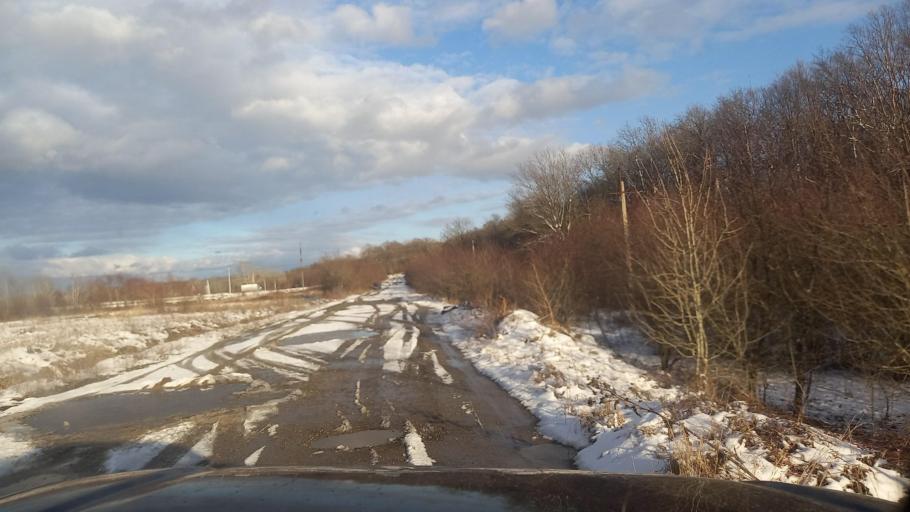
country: RU
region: Krasnodarskiy
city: Smolenskaya
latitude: 44.7708
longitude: 38.8139
